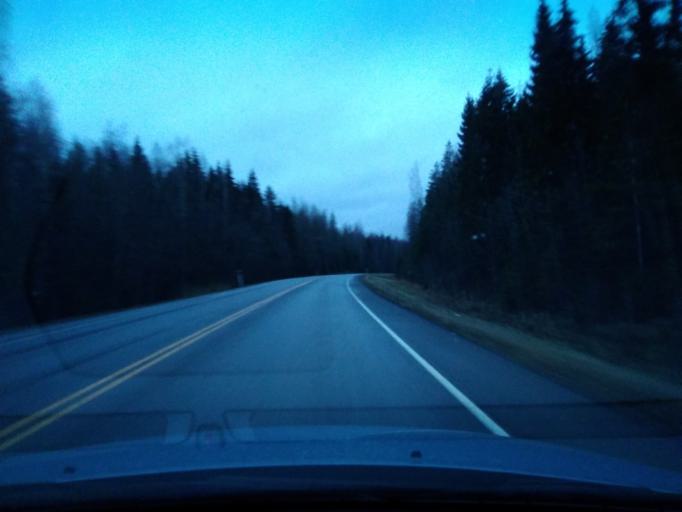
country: FI
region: Uusimaa
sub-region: Porvoo
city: Porvoo
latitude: 60.4340
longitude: 25.5747
